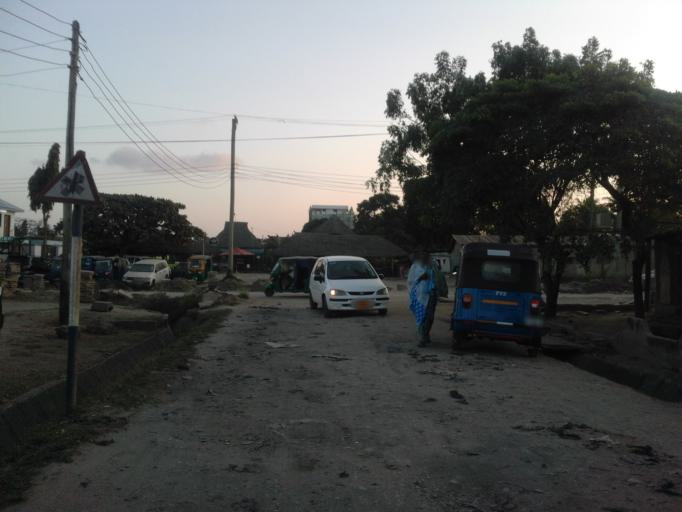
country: TZ
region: Dar es Salaam
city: Magomeni
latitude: -6.7785
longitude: 39.2374
